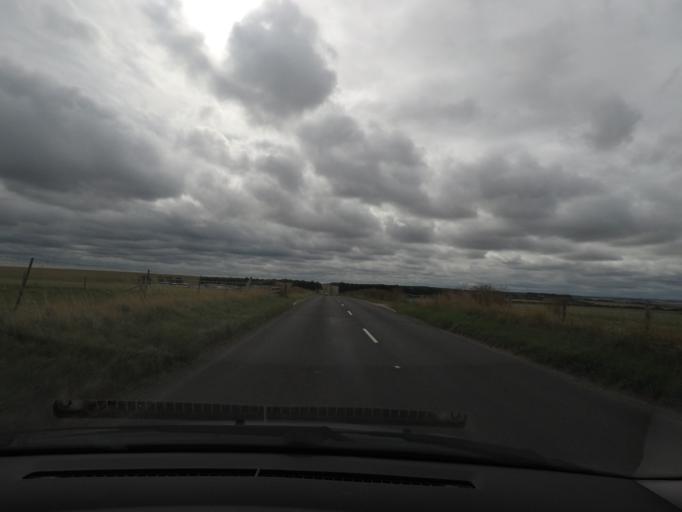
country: GB
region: England
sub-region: Wiltshire
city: Shrewton
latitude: 51.1885
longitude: -1.8610
